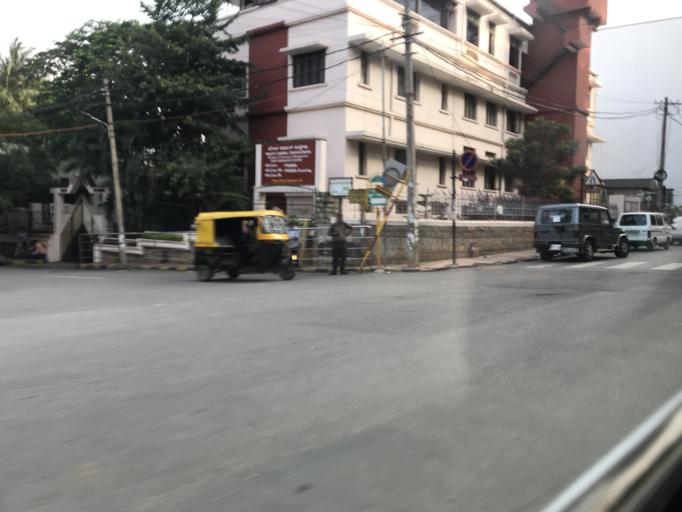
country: IN
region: Karnataka
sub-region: Bangalore Urban
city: Bangalore
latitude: 12.9932
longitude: 77.5889
